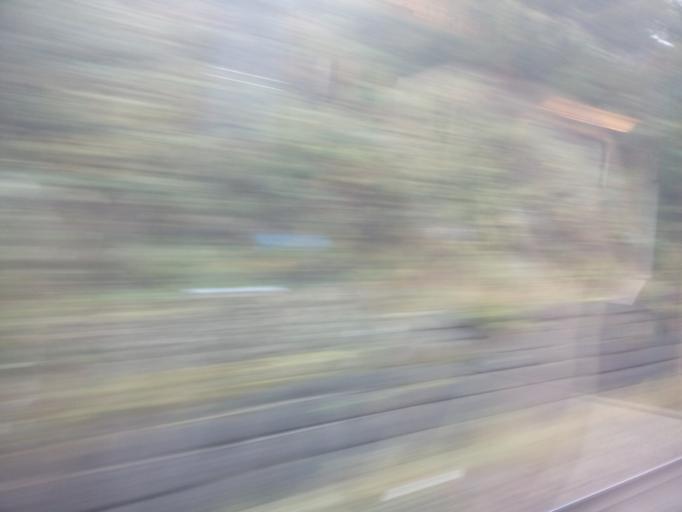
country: GB
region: England
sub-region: City and Borough of Leeds
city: Leeds
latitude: 53.7927
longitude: -1.5156
